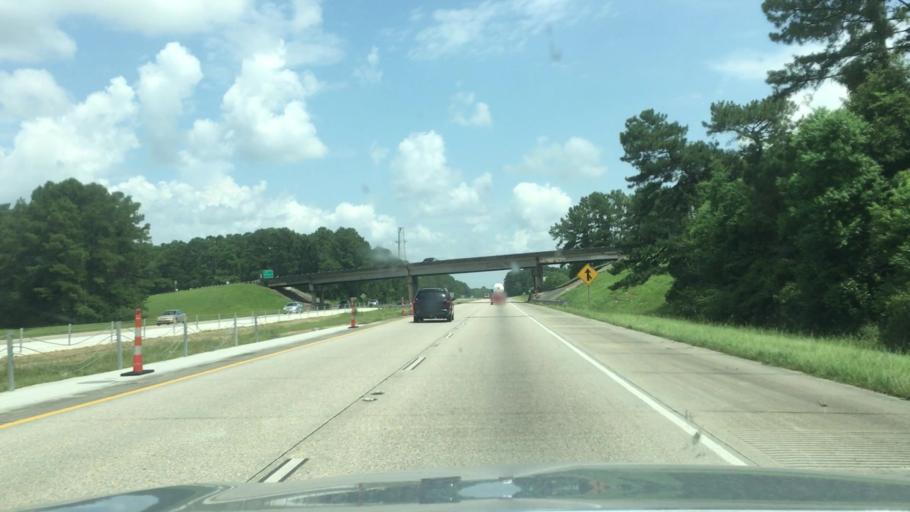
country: US
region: Louisiana
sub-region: Saint Tammany Parish
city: Pearl River
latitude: 30.3519
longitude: -89.7401
